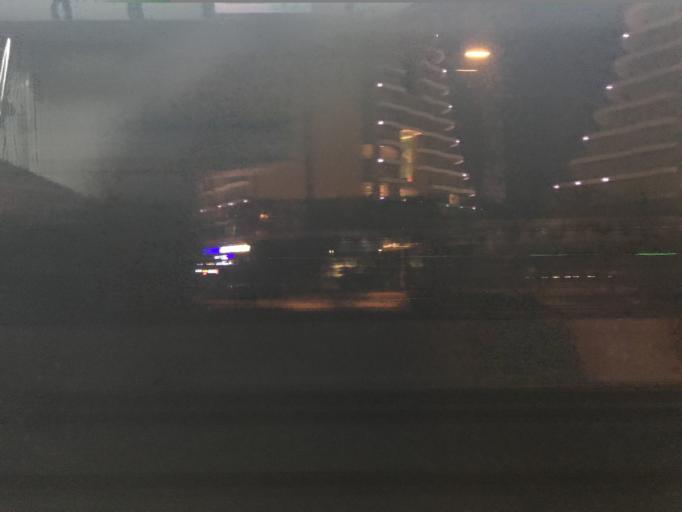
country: TR
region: Istanbul
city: Pendik
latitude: 40.8855
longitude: 29.2083
